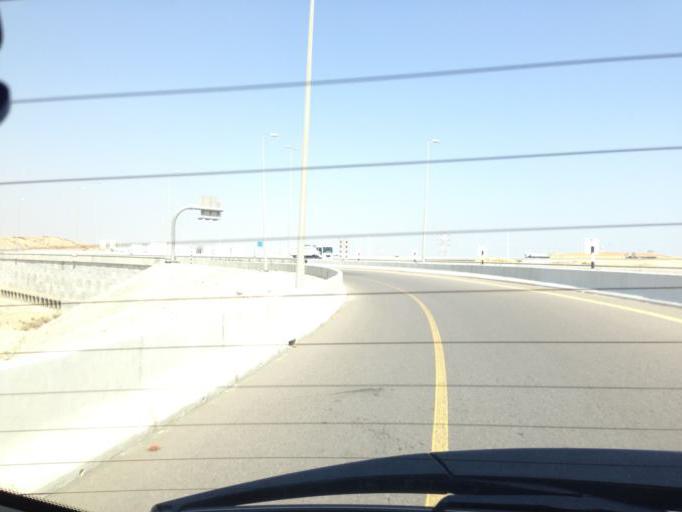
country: OM
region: Muhafazat Masqat
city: As Sib al Jadidah
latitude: 23.5657
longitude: 58.1918
